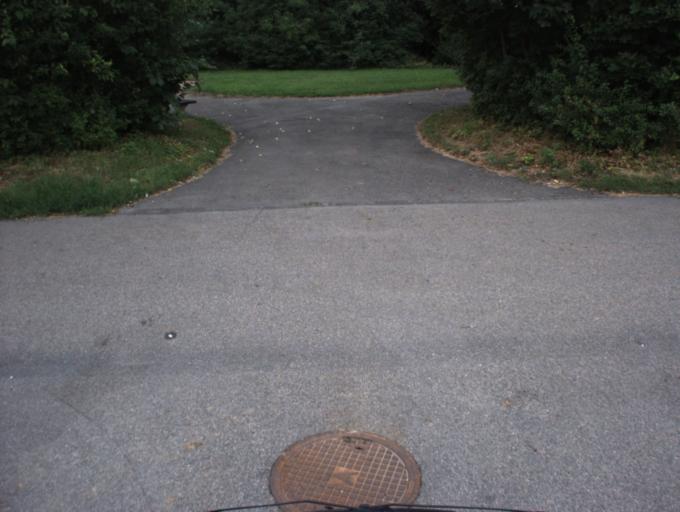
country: SE
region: Skane
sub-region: Helsingborg
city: Morarp
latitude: 56.0535
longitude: 12.8757
